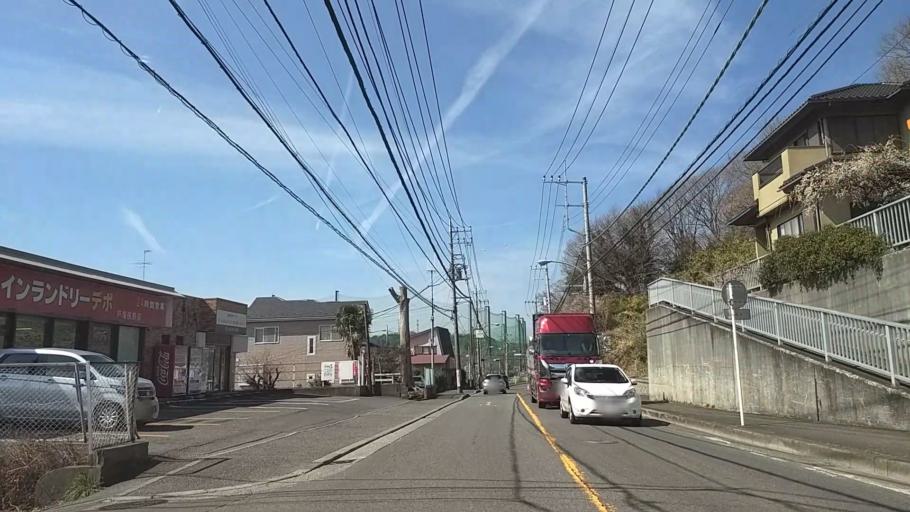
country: JP
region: Kanagawa
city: Fujisawa
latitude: 35.3806
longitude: 139.4951
